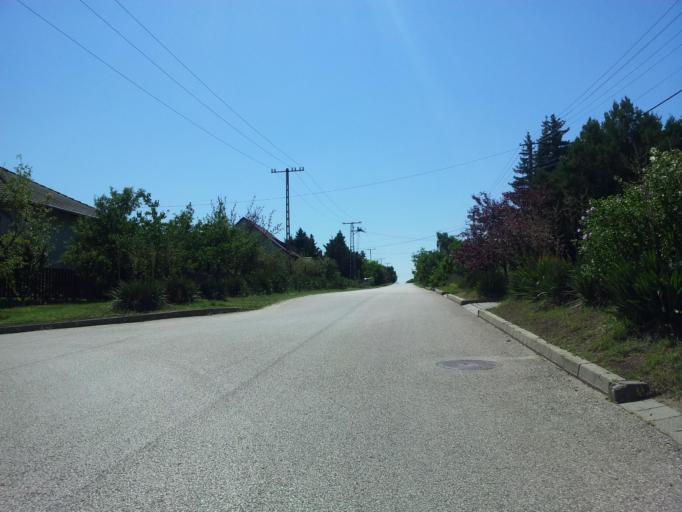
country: HU
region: Pest
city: Veresegyhaz
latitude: 47.6583
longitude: 19.2760
